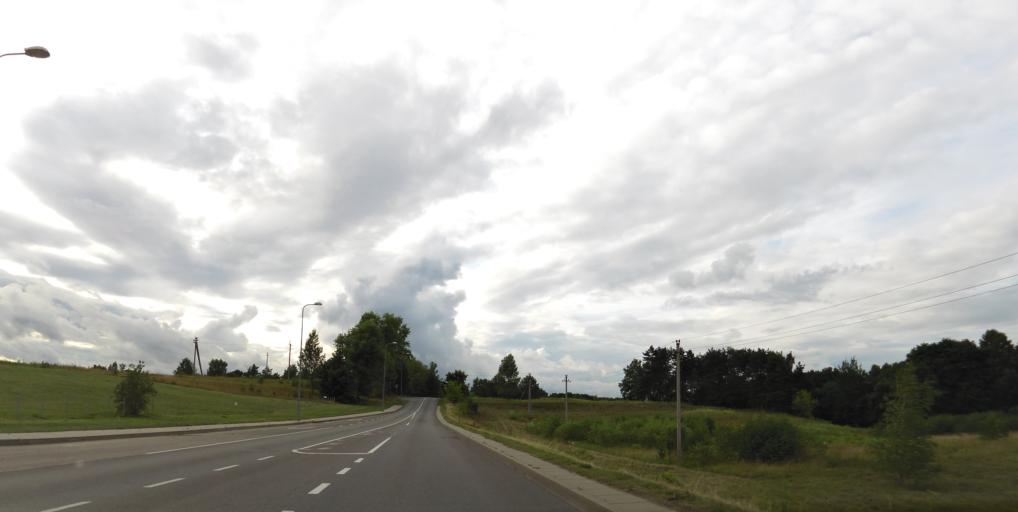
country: LT
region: Vilnius County
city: Justiniskes
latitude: 54.7095
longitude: 25.2021
